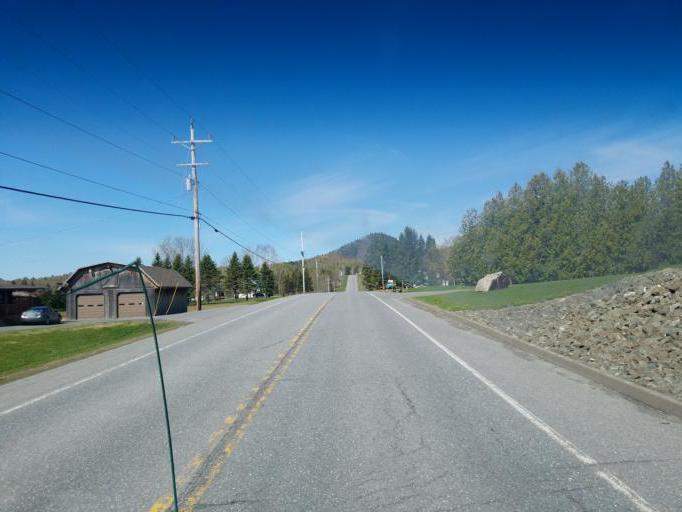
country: US
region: Maine
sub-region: Aroostook County
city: Presque Isle
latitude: 46.6667
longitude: -68.2121
